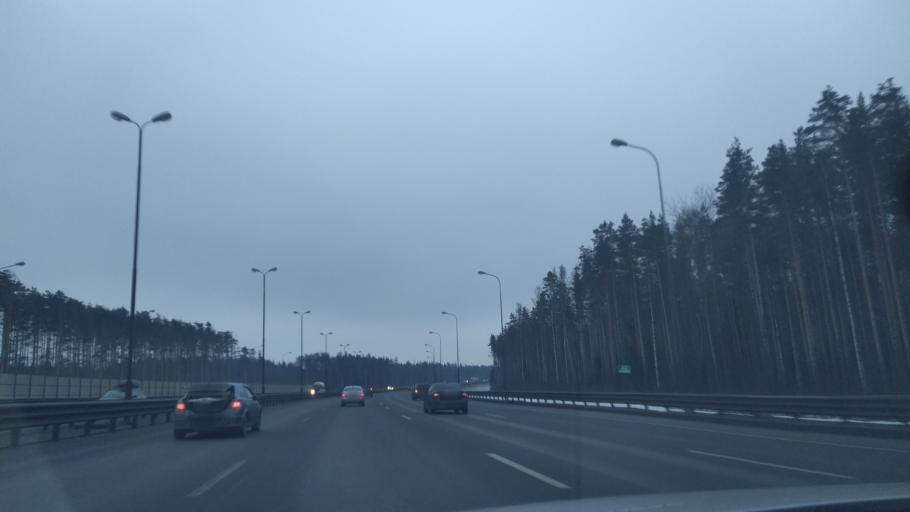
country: RU
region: St.-Petersburg
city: Krasnogvargeisky
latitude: 59.9710
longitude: 30.5484
